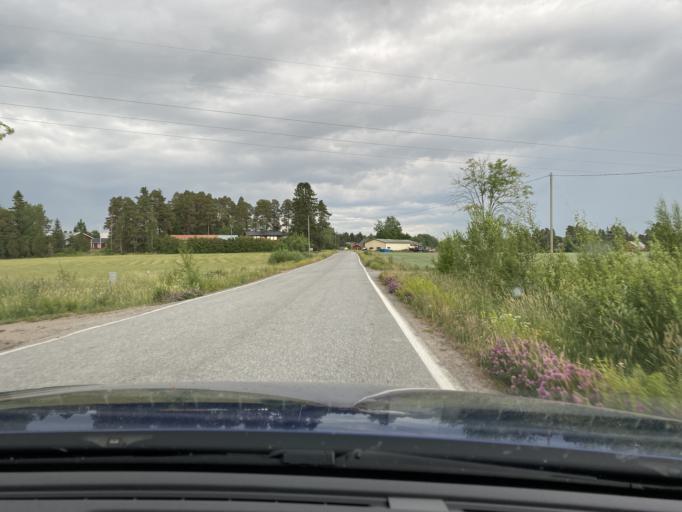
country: FI
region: Satakunta
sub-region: Rauma
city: Eura
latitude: 61.1571
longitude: 22.0999
